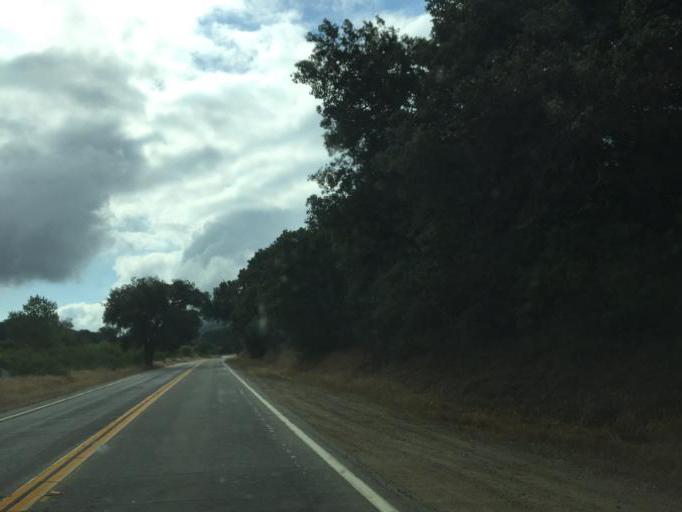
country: US
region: California
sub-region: Los Angeles County
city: Leona Valley
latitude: 34.5835
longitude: -118.3493
